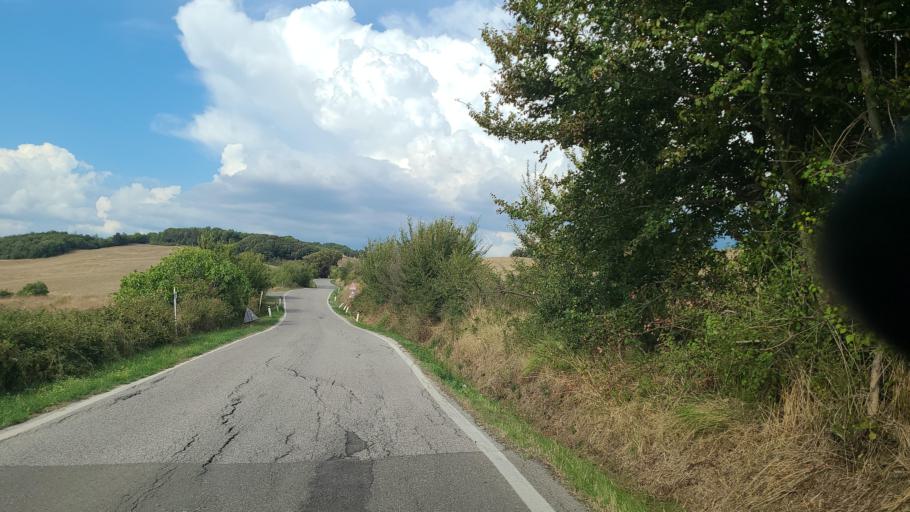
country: IT
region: Tuscany
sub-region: Provincia di Siena
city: San Gimignano
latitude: 43.4060
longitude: 10.9749
